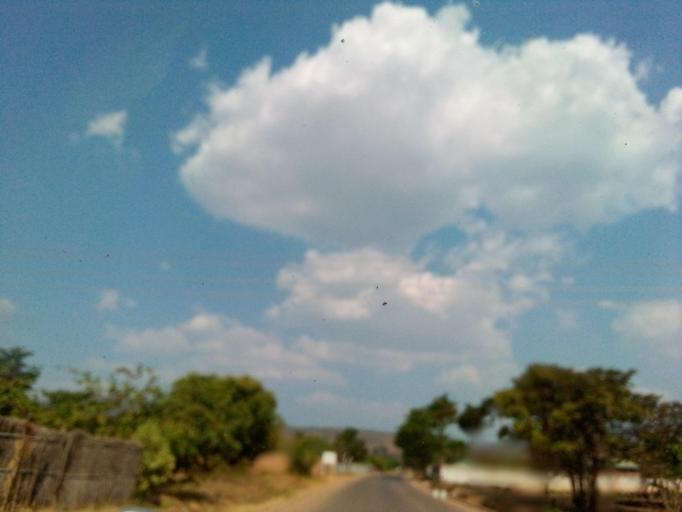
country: ZM
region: Northern
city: Mpika
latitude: -11.8451
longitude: 31.4466
